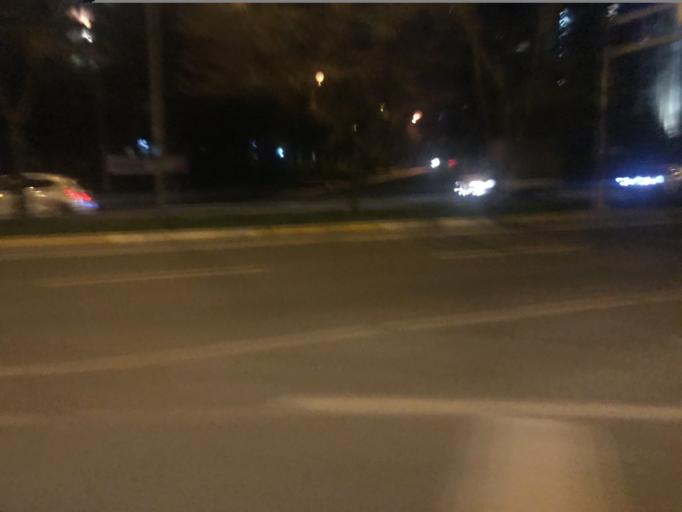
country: TR
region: Istanbul
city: Bahcelievler
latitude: 40.9771
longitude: 28.8518
